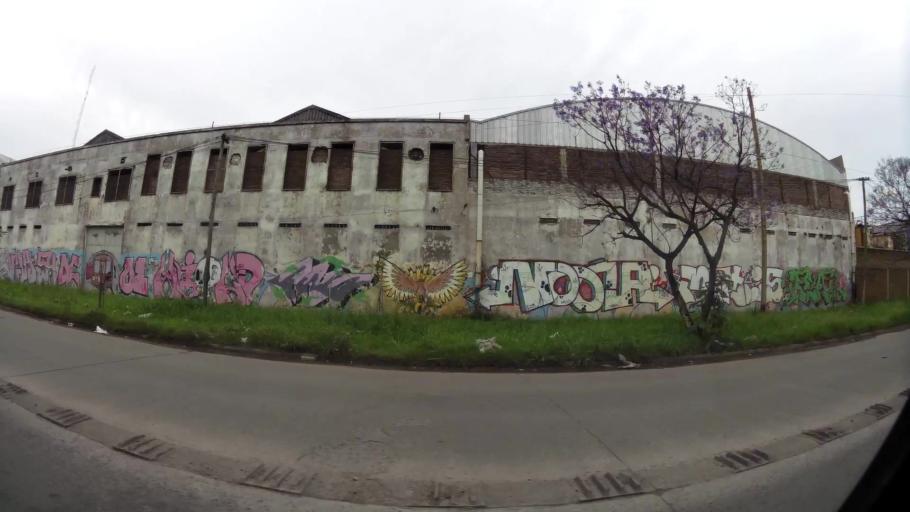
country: AR
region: Buenos Aires
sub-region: Partido de Lanus
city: Lanus
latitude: -34.7123
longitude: -58.3636
